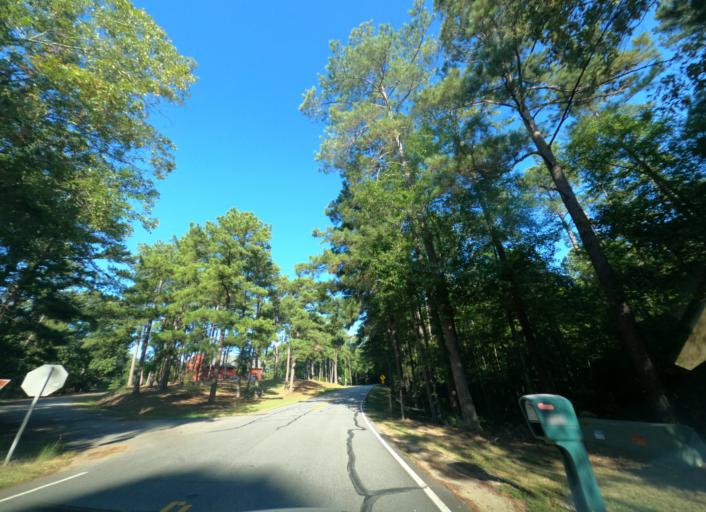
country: US
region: Georgia
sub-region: Lincoln County
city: Lincolnton
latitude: 33.8825
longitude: -82.4133
